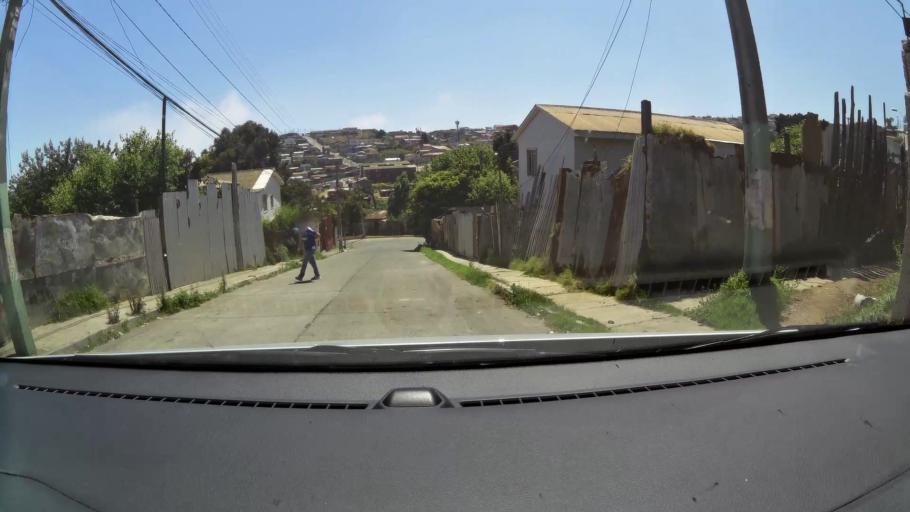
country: CL
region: Valparaiso
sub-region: Provincia de Valparaiso
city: Valparaiso
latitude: -33.0337
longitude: -71.6508
